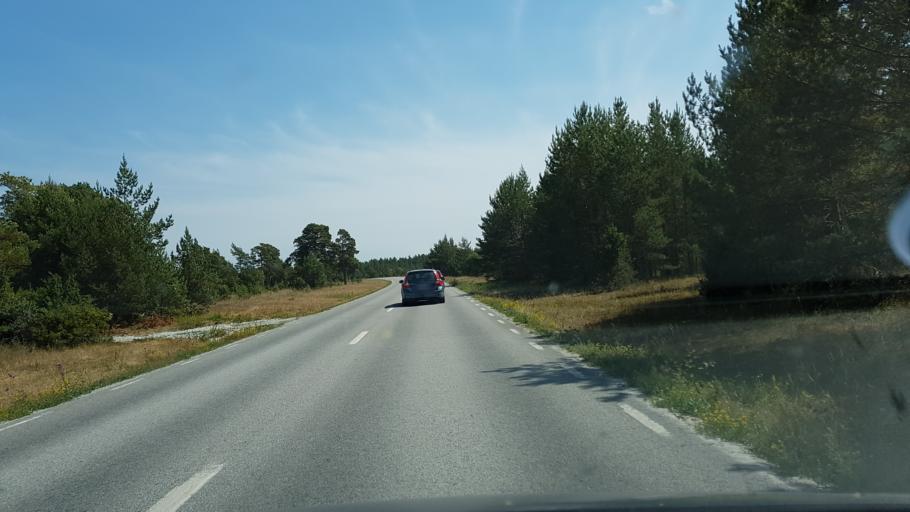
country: SE
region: Gotland
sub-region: Gotland
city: Visby
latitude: 57.6354
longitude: 18.4046
